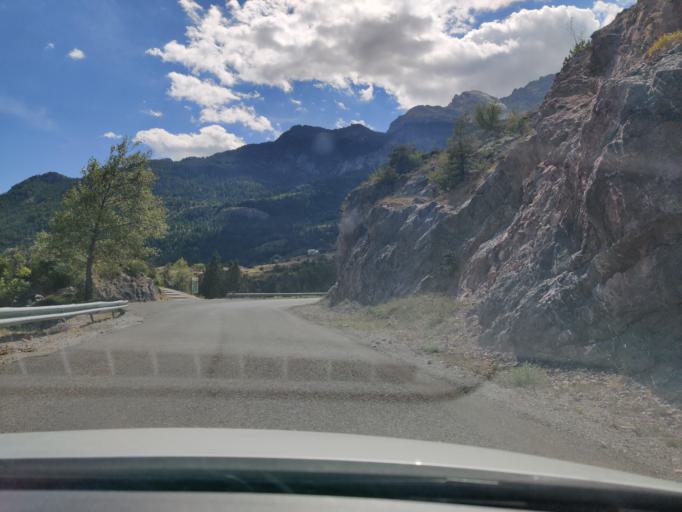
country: FR
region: Provence-Alpes-Cote d'Azur
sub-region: Departement des Hautes-Alpes
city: Saint-Martin-de-Queyrieres
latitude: 44.7394
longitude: 6.5721
